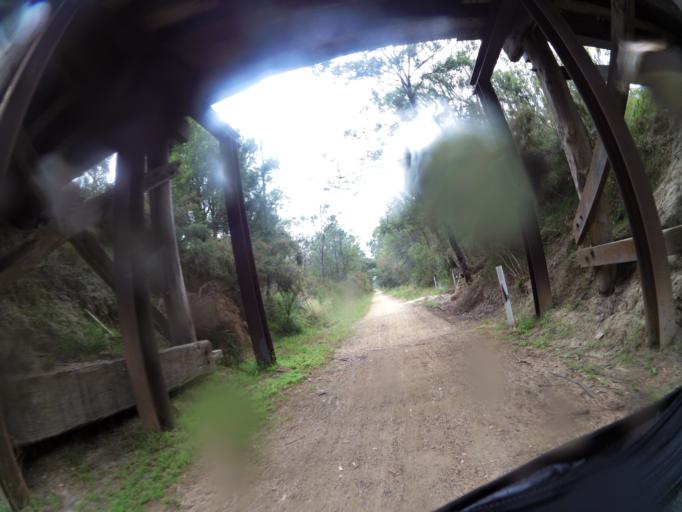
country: AU
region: Victoria
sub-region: East Gippsland
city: Bairnsdale
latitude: -37.7435
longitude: 147.8096
